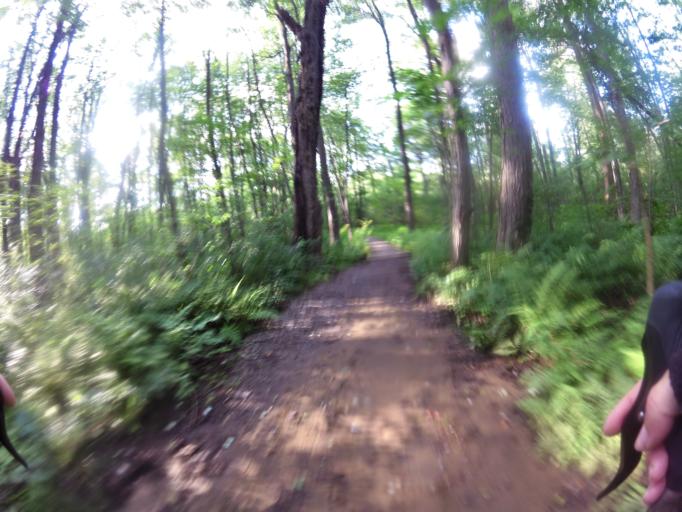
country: CA
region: Ontario
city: Ottawa
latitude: 45.3241
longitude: -75.7281
